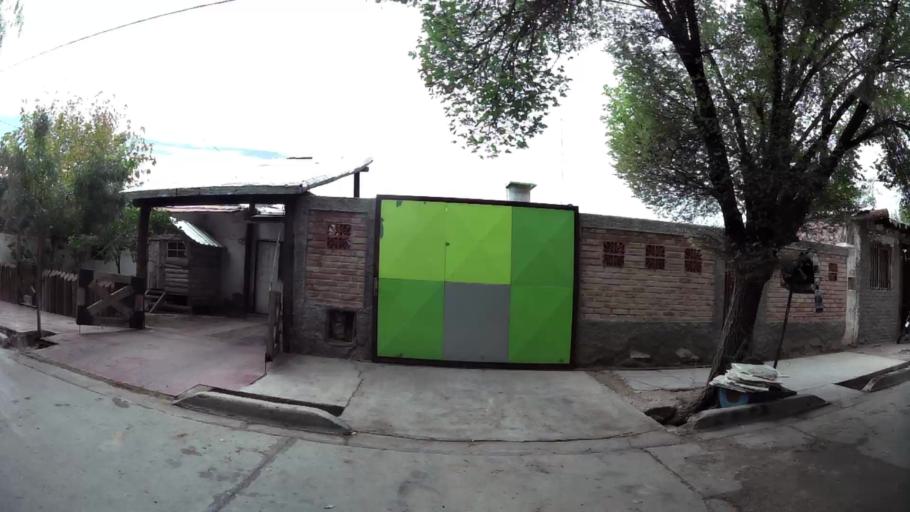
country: AR
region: Mendoza
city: Las Heras
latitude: -32.8599
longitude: -68.8694
